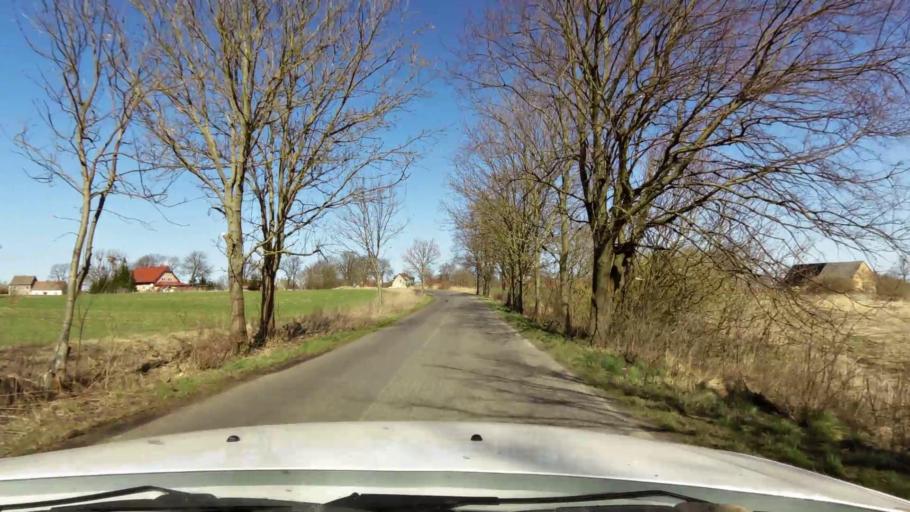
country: PL
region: West Pomeranian Voivodeship
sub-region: Powiat gryfinski
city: Cedynia
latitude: 52.8821
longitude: 14.2866
